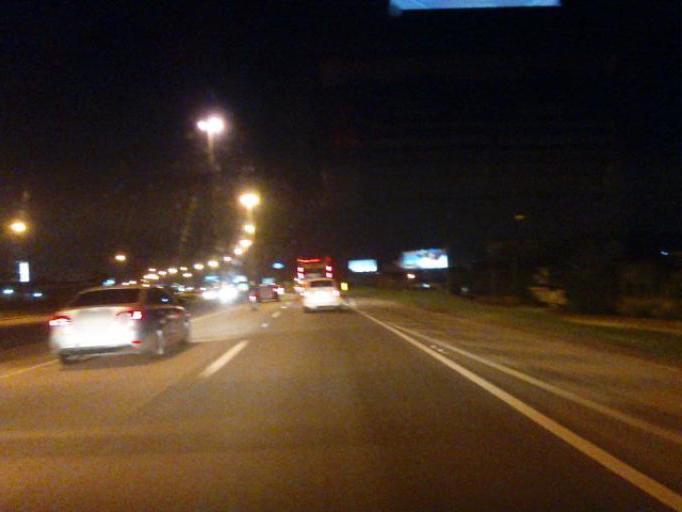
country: BR
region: Santa Catarina
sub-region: Balneario Camboriu
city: Balneario Camboriu
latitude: -26.9950
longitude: -48.6583
